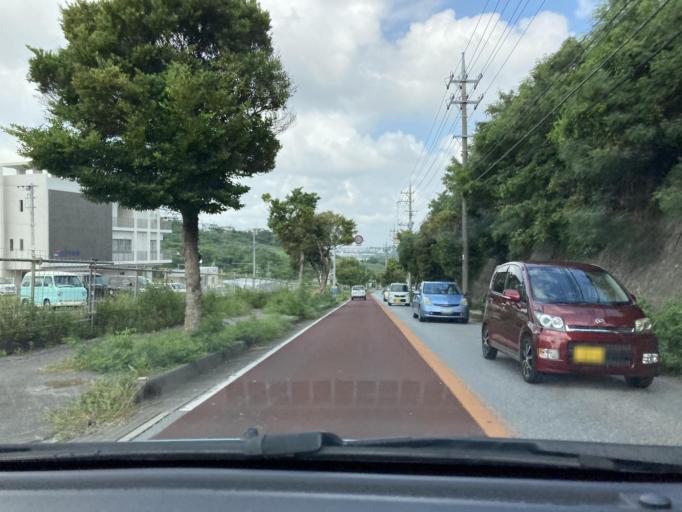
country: JP
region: Okinawa
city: Ginowan
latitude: 26.2266
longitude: 127.7361
